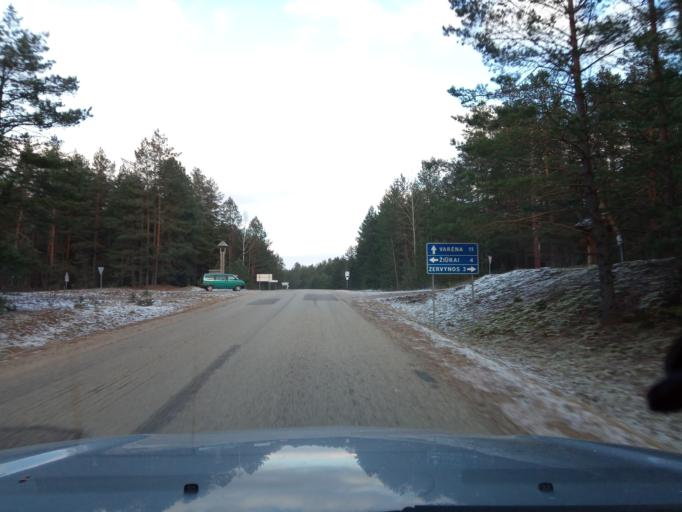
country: LT
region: Alytaus apskritis
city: Varena
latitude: 54.1318
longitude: 24.4646
